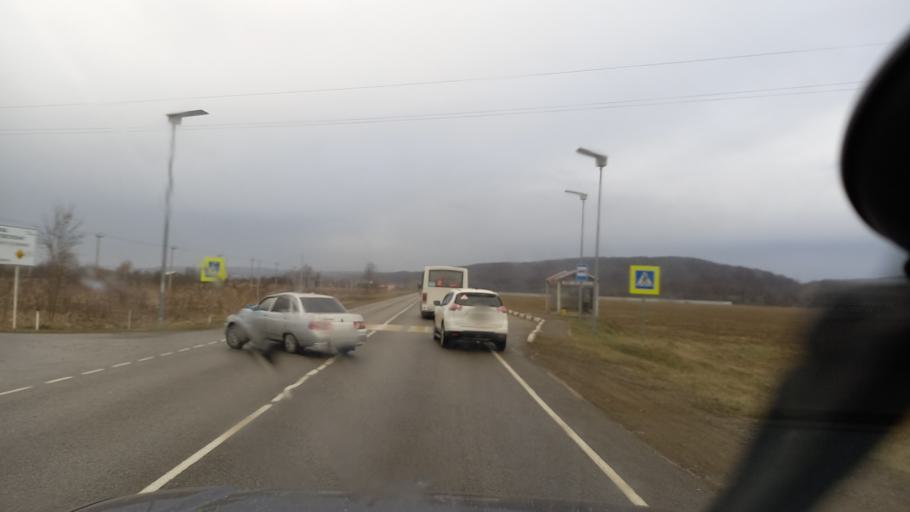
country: RU
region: Adygeya
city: Tul'skiy
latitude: 44.5319
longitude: 40.1382
